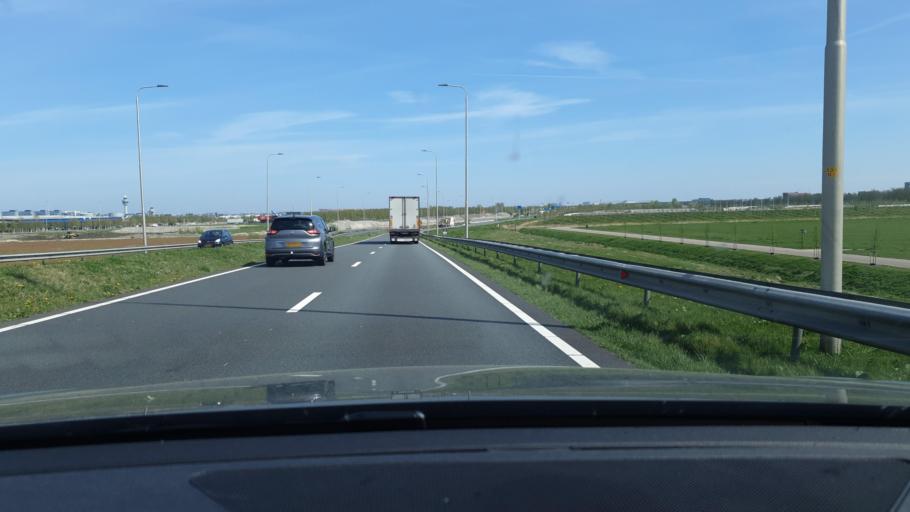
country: NL
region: North Holland
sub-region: Gemeente Aalsmeer
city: Aalsmeer
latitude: 52.2810
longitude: 4.7471
